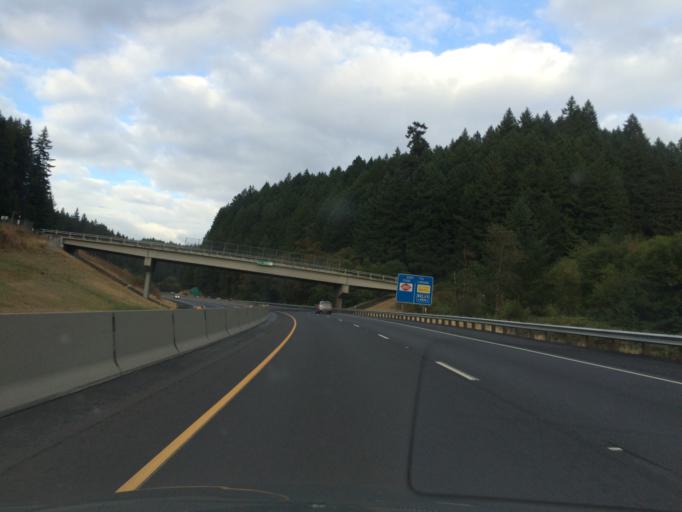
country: US
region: Oregon
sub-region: Lane County
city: Cottage Grove
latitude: 43.7515
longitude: -123.1462
